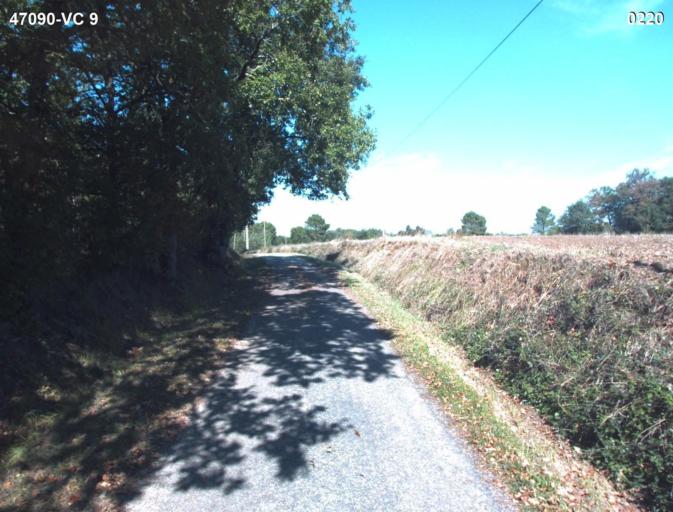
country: FR
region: Aquitaine
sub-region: Departement du Lot-et-Garonne
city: Nerac
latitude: 44.1848
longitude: 0.3875
